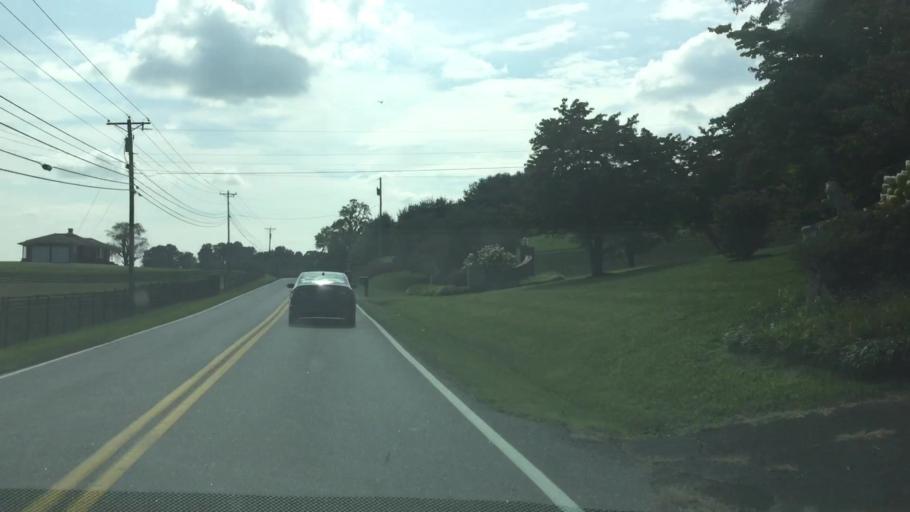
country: US
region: Tennessee
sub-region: Sullivan County
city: Fairmount
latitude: 36.6031
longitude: -82.1036
